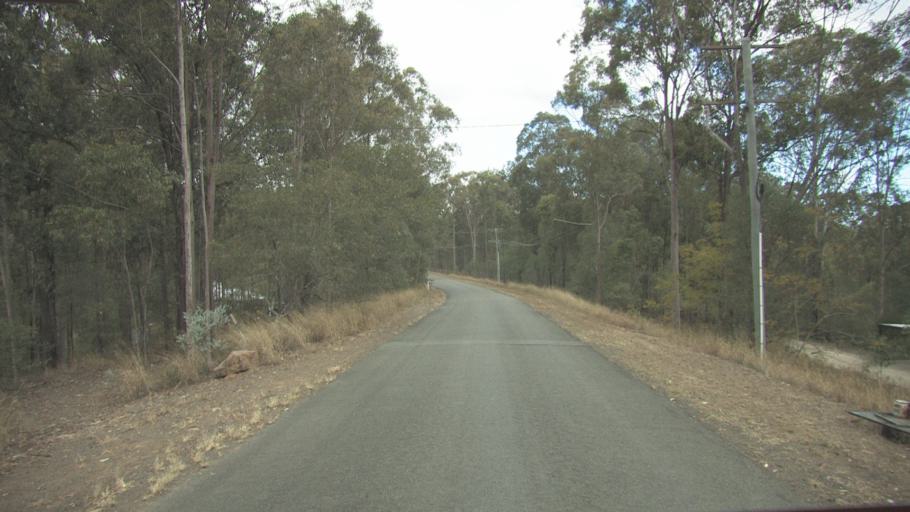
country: AU
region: Queensland
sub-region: Logan
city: Cedar Vale
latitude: -27.8936
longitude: 153.0248
